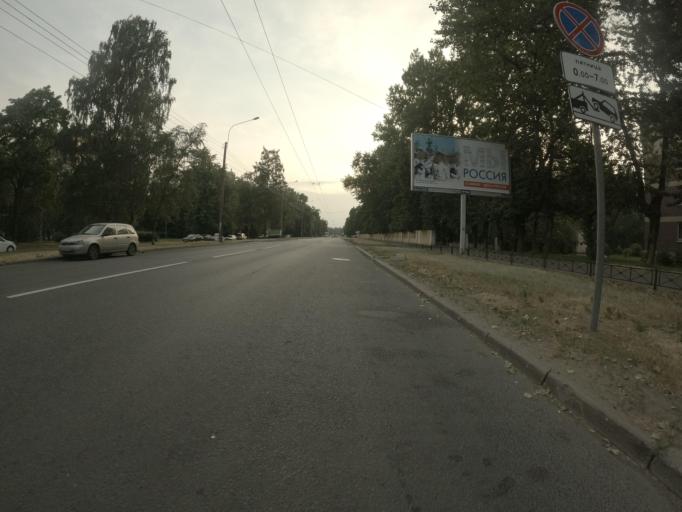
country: RU
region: Leningrad
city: Kalininskiy
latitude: 59.9856
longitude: 30.4103
